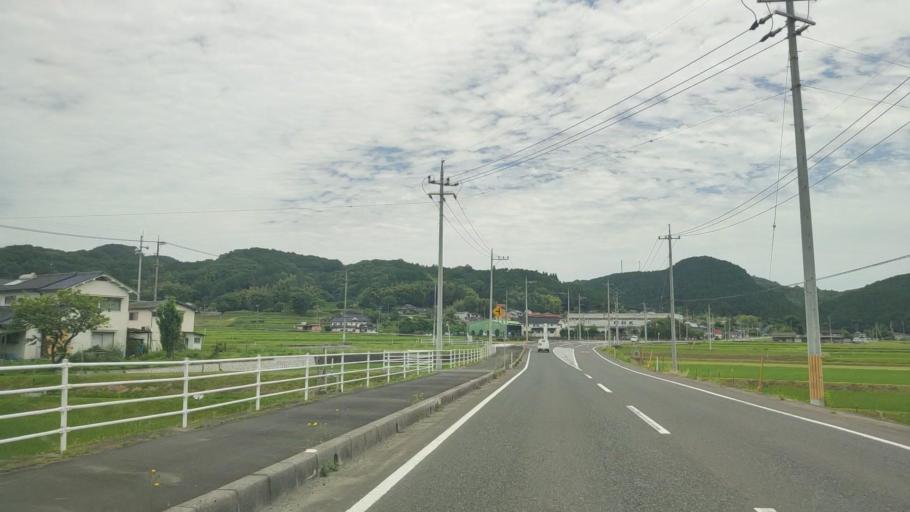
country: JP
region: Okayama
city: Tsuyama
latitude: 35.0640
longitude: 134.2066
